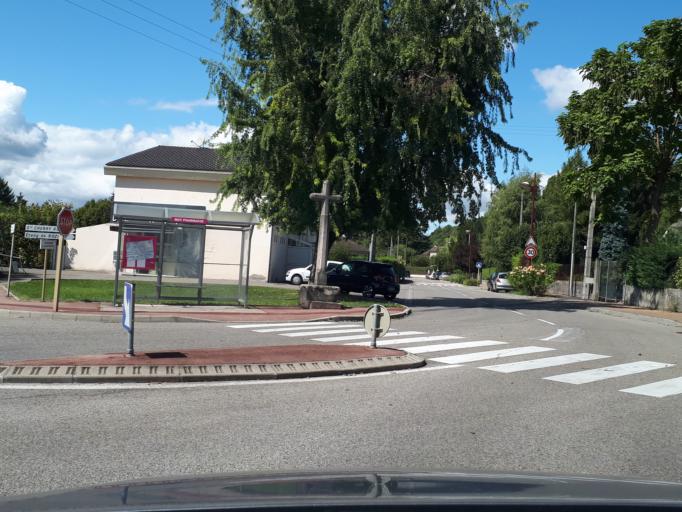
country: FR
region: Rhone-Alpes
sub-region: Departement de l'Isere
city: Ruy
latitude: 45.5884
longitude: 5.3097
